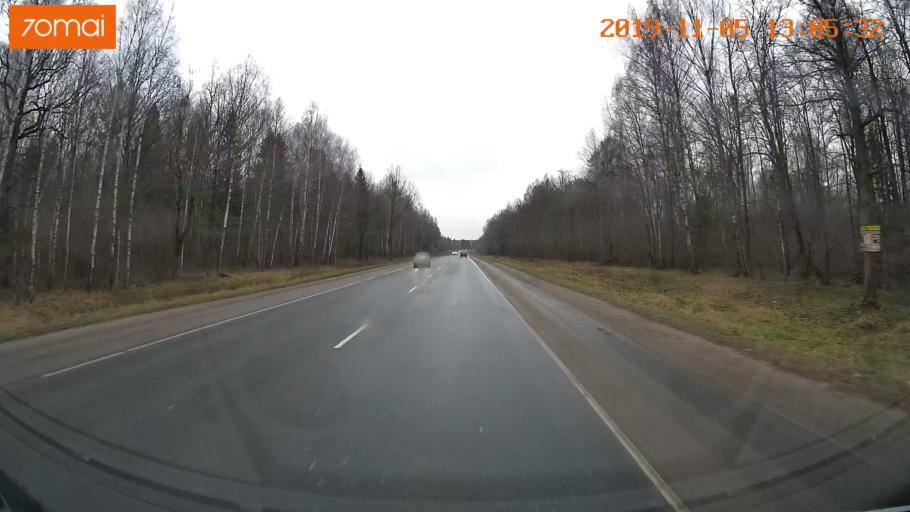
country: RU
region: Ivanovo
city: Kitovo
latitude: 56.8819
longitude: 41.2450
